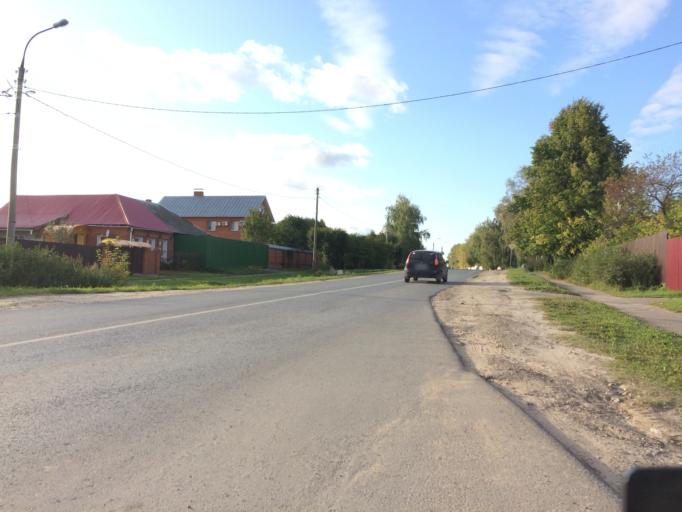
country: RU
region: Mariy-El
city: Yoshkar-Ola
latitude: 56.6512
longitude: 47.9797
